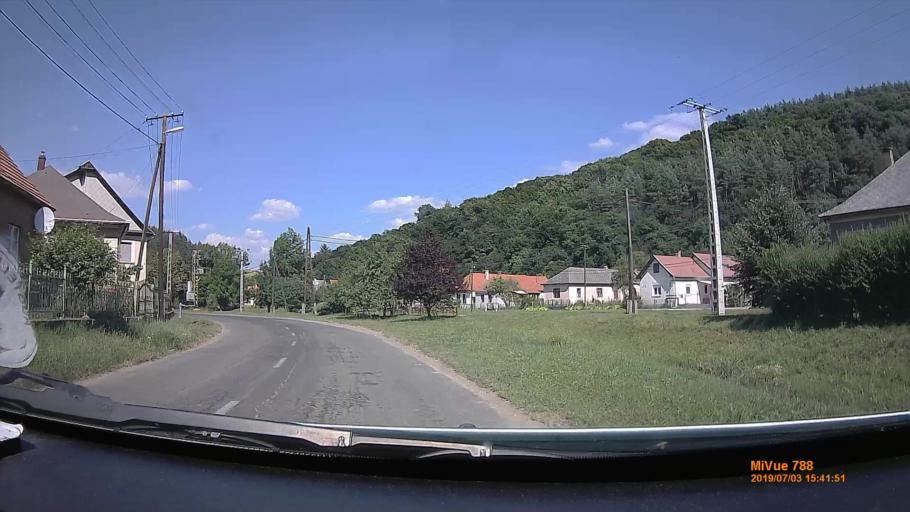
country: HU
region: Heves
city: Szilvasvarad
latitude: 48.1669
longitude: 20.4267
